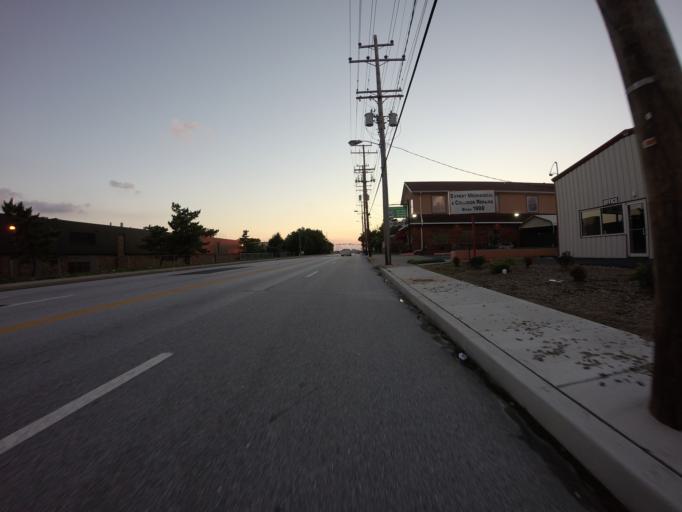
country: US
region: Maryland
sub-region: Baltimore County
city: Dundalk
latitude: 39.2722
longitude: -76.5418
